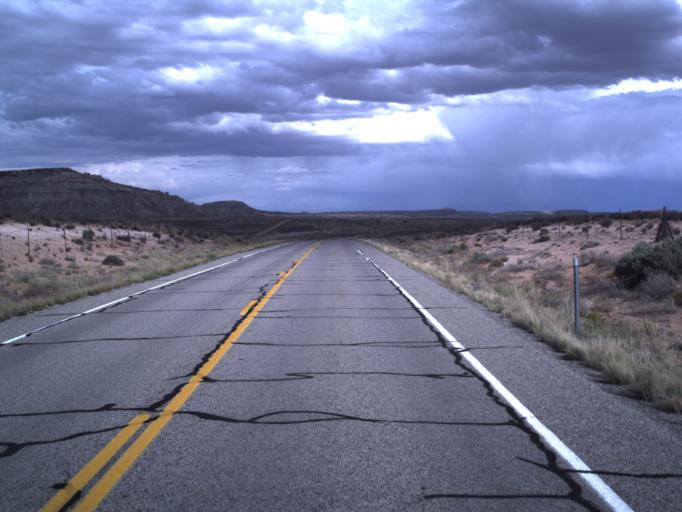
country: US
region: Utah
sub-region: San Juan County
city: Blanding
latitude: 37.2978
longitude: -109.4712
